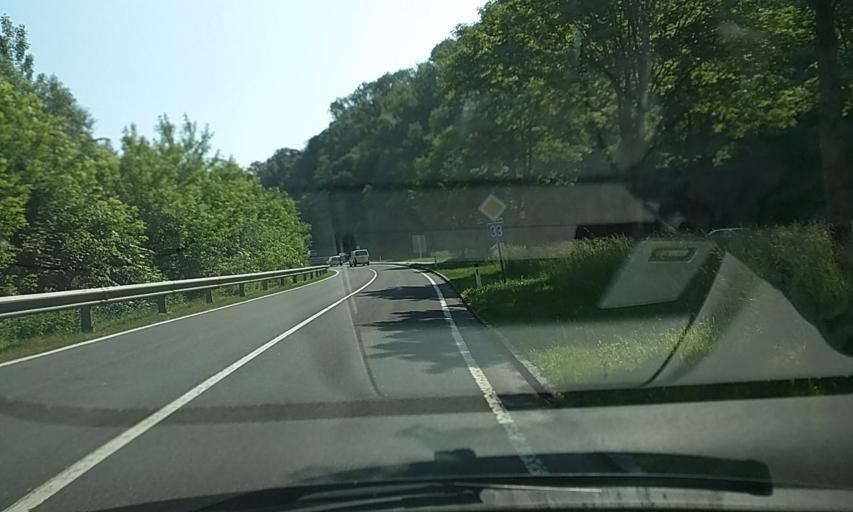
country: AT
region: Lower Austria
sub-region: Politischer Bezirk Melk
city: Melk
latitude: 48.2313
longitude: 15.3344
